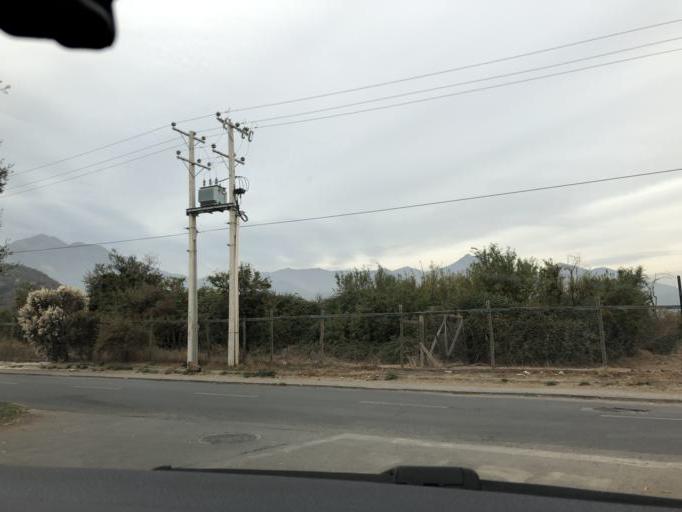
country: CL
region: Santiago Metropolitan
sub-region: Provincia de Cordillera
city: Puente Alto
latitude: -33.5899
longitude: -70.5101
